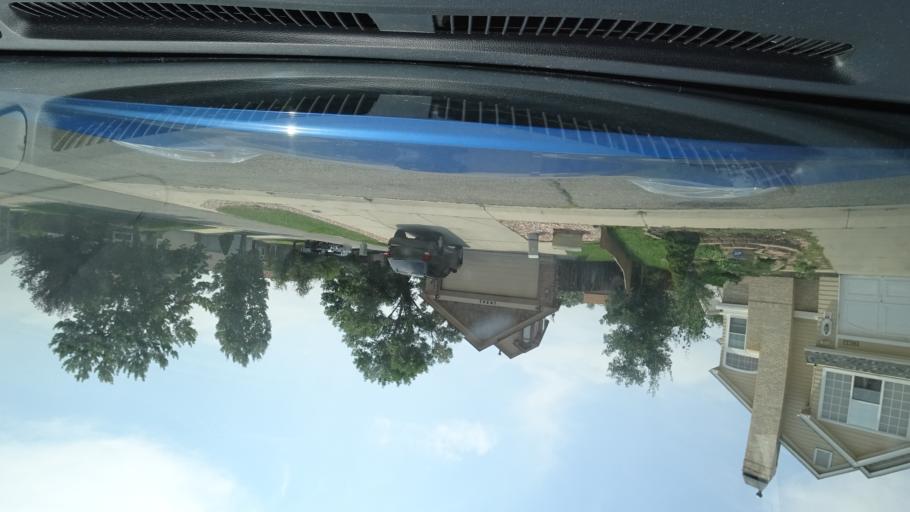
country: US
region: Colorado
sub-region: Adams County
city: Aurora
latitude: 39.7745
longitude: -104.7575
